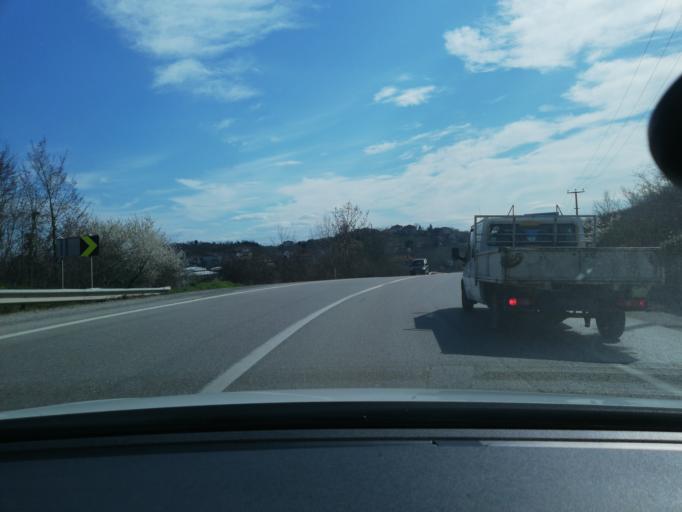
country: TR
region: Duzce
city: Akcakoca
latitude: 41.0875
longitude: 31.1500
